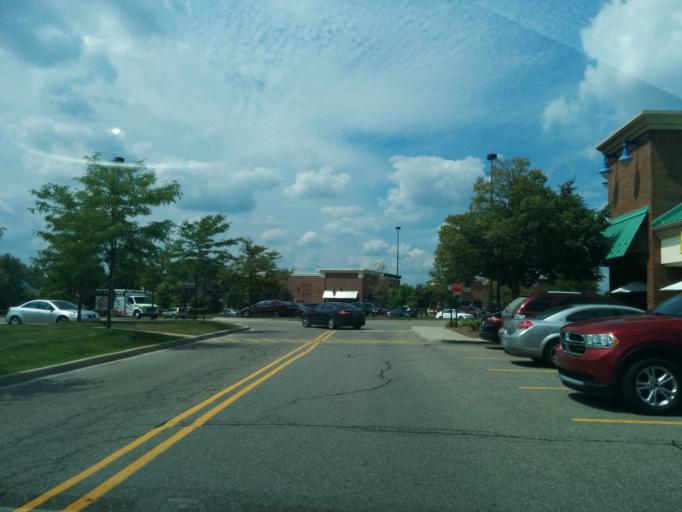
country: US
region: Michigan
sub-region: Oakland County
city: Novi
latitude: 42.4811
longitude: -83.4733
